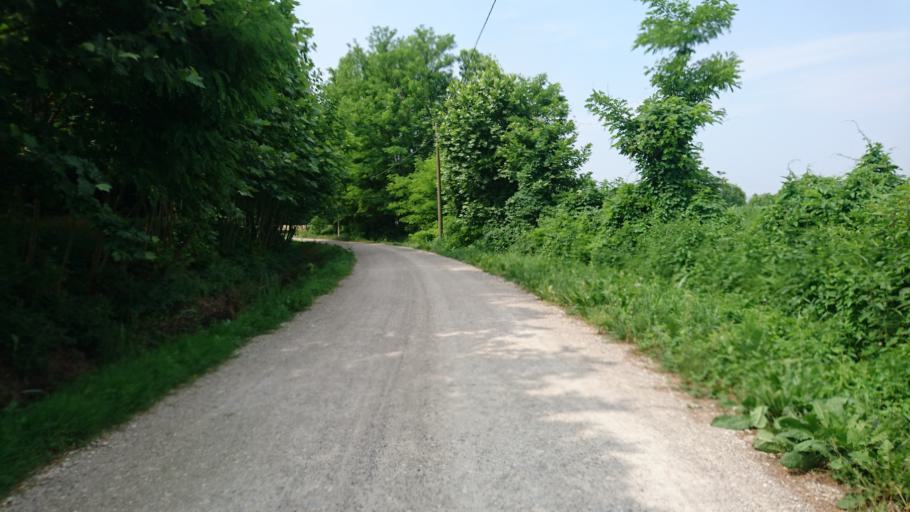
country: IT
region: Veneto
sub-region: Provincia di Padova
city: Legnaro
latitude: 45.3292
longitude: 11.9574
